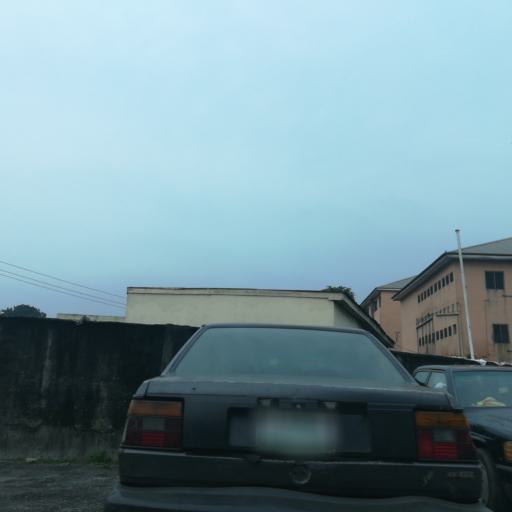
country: NG
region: Rivers
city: Port Harcourt
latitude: 4.7661
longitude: 7.0124
